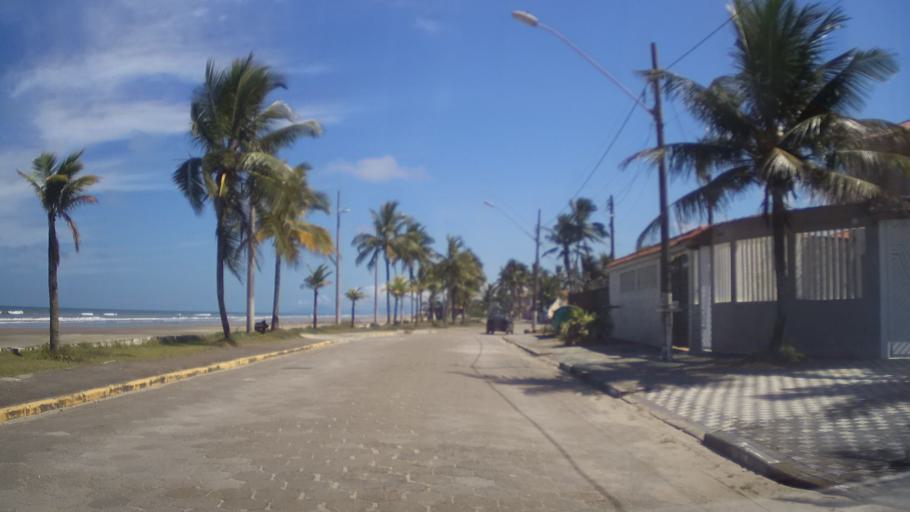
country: BR
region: Sao Paulo
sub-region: Itanhaem
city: Itanhaem
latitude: -24.1418
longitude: -46.7076
